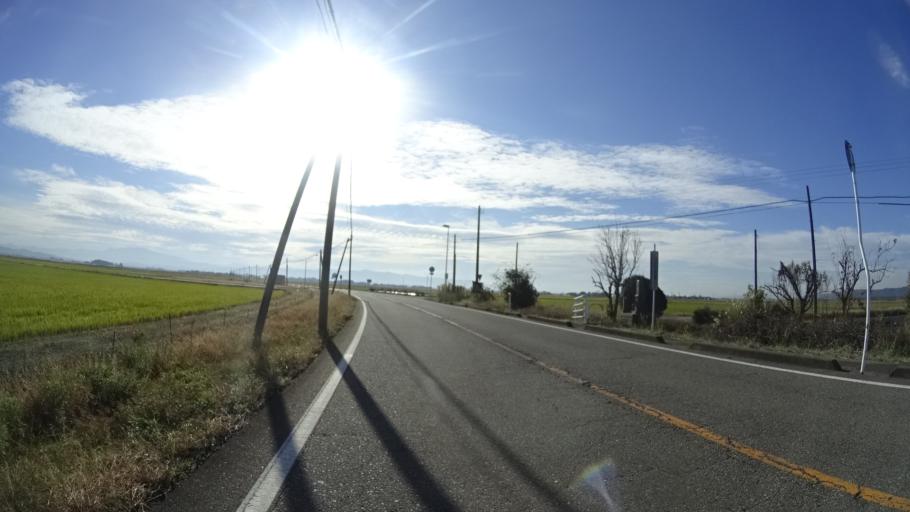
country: JP
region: Niigata
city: Mitsuke
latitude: 37.5704
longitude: 138.8417
